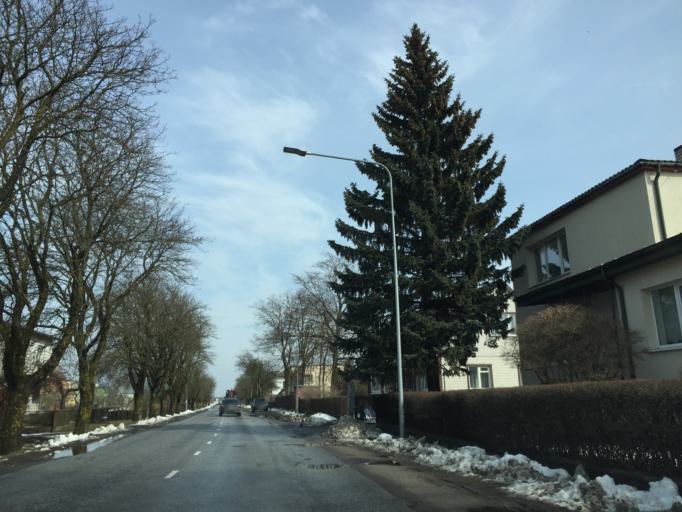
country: EE
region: Saare
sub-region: Kuressaare linn
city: Kuressaare
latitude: 58.2531
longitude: 22.4765
